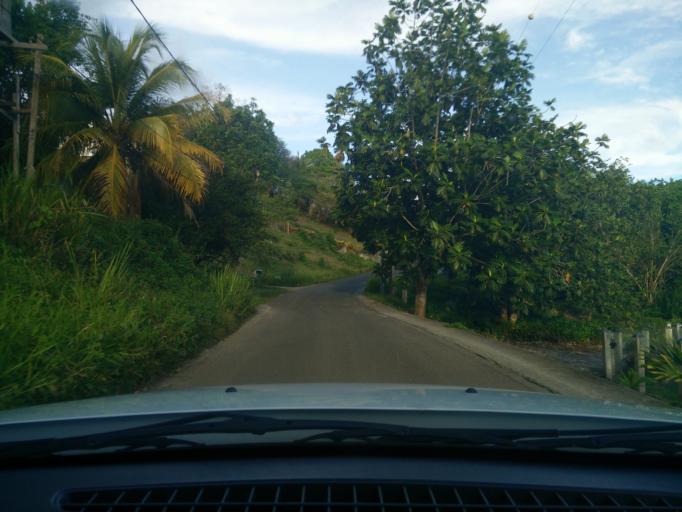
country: GP
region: Guadeloupe
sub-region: Guadeloupe
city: Les Abymes
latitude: 16.2498
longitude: -61.4968
